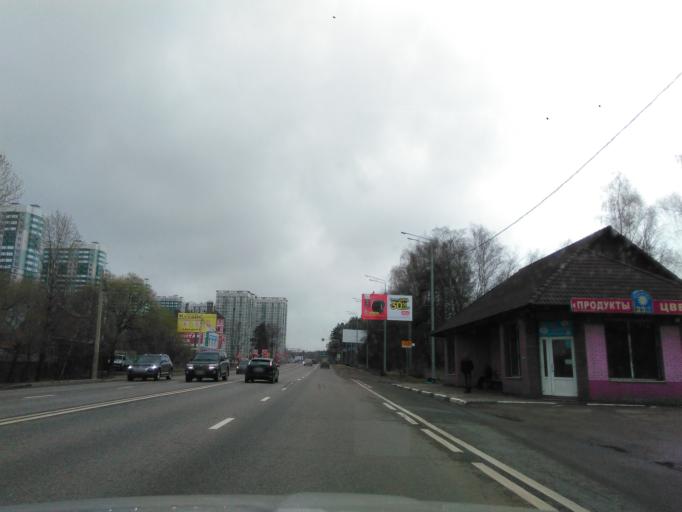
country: RU
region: Moskovskaya
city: Opalikha
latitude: 55.8373
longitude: 37.2596
